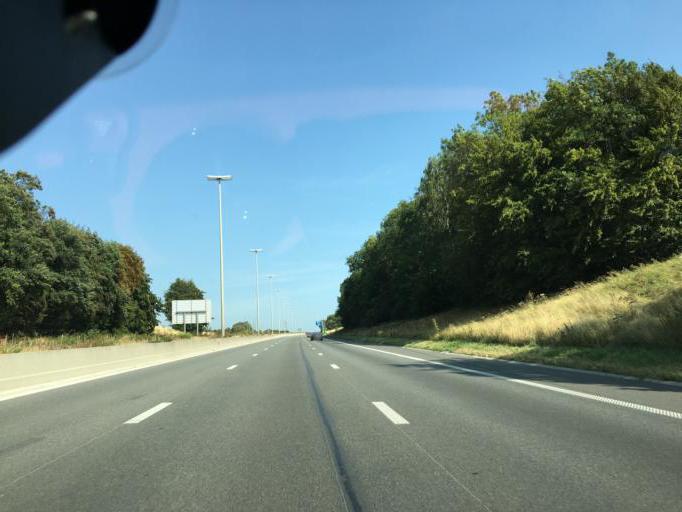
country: BE
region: Wallonia
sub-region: Province de Namur
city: Gembloux
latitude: 50.4956
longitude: 4.7108
